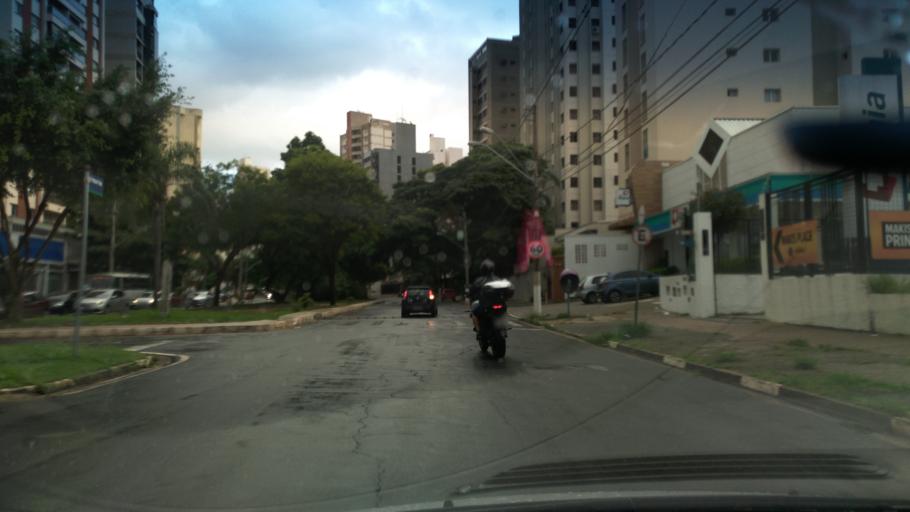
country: BR
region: Sao Paulo
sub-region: Campinas
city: Campinas
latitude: -22.9114
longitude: -47.0451
